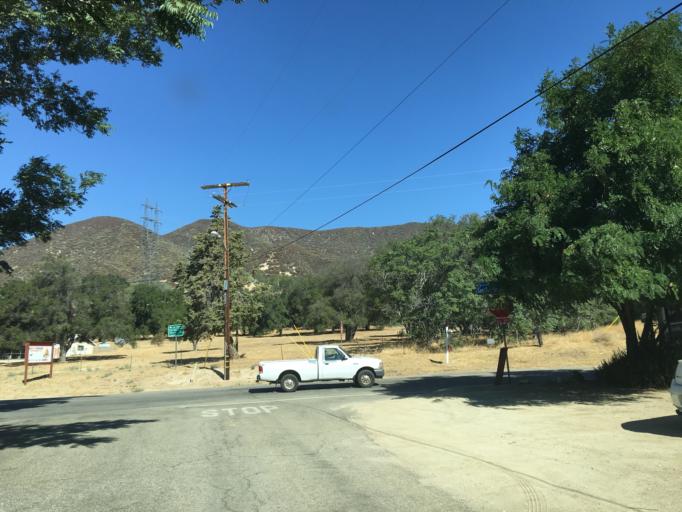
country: US
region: California
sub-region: Los Angeles County
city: Green Valley
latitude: 34.6219
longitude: -118.4137
